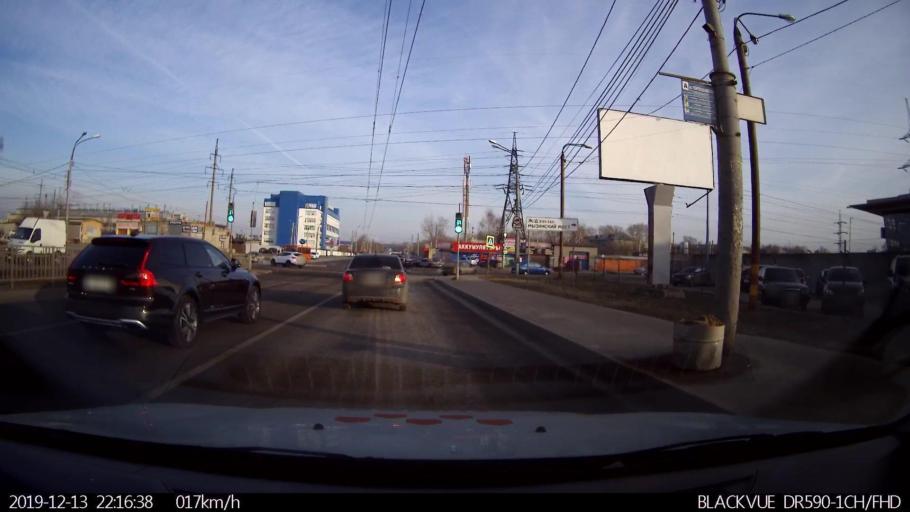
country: RU
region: Nizjnij Novgorod
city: Nizhniy Novgorod
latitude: 56.2637
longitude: 43.9031
